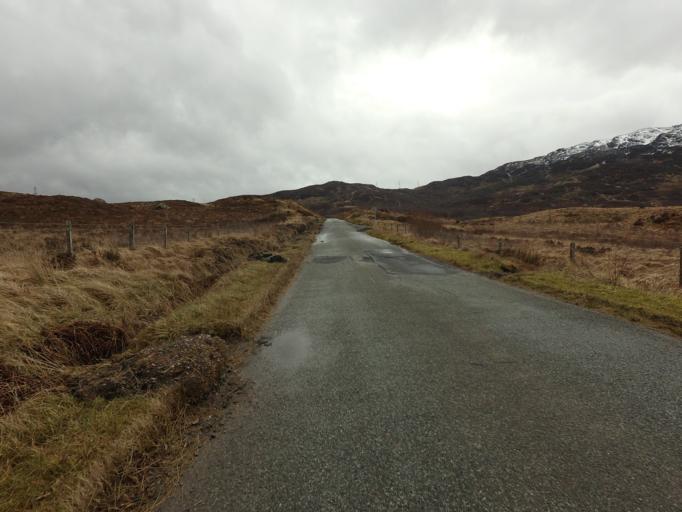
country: GB
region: Scotland
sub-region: West Dunbartonshire
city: Balloch
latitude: 56.2523
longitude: -4.5888
